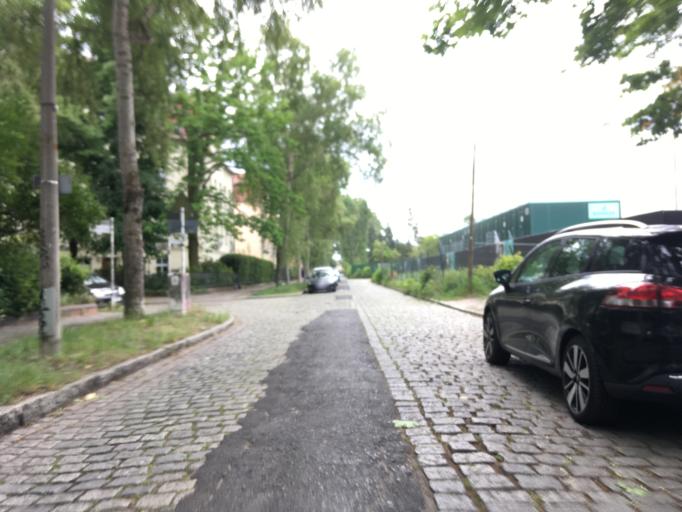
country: DE
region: Berlin
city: Karlshorst
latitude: 52.4814
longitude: 13.5121
